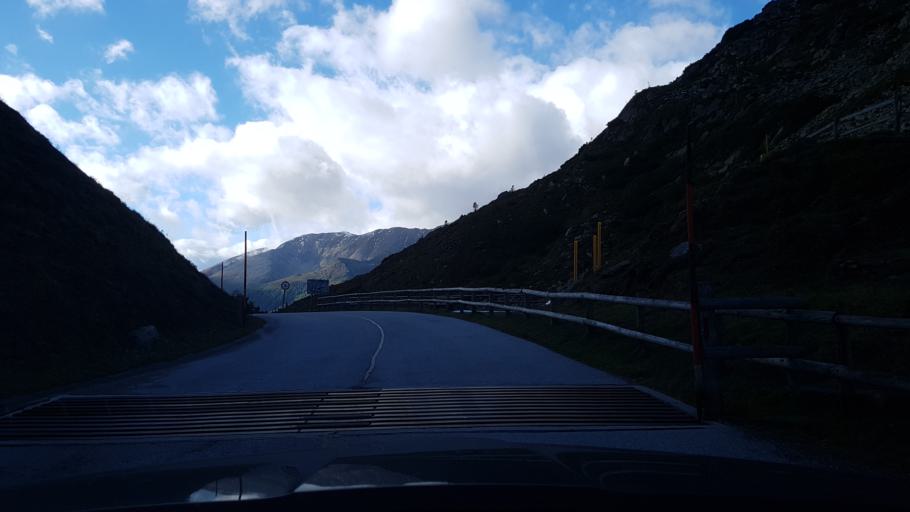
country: AT
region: Styria
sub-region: Politischer Bezirk Liezen
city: Sankt Nikolai im Solktal
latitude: 47.2719
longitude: 14.0798
